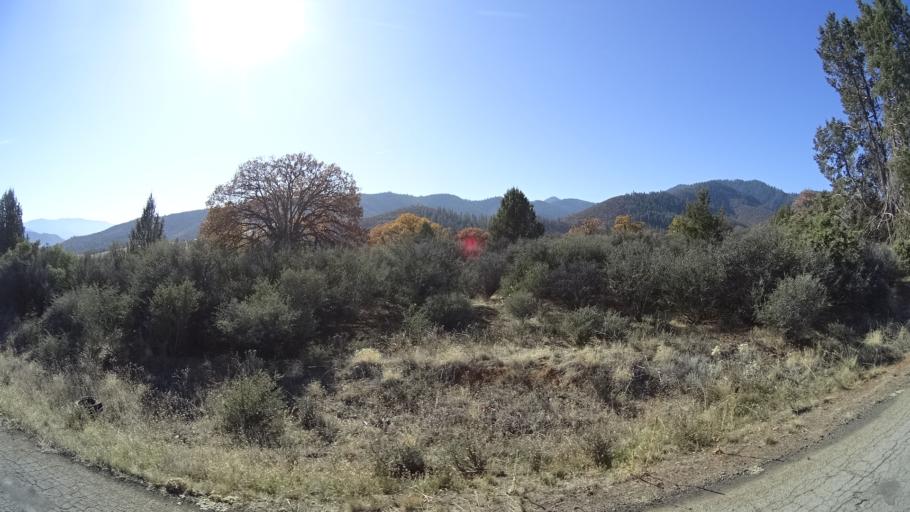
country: US
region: California
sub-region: Siskiyou County
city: Yreka
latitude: 41.7731
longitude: -122.6366
